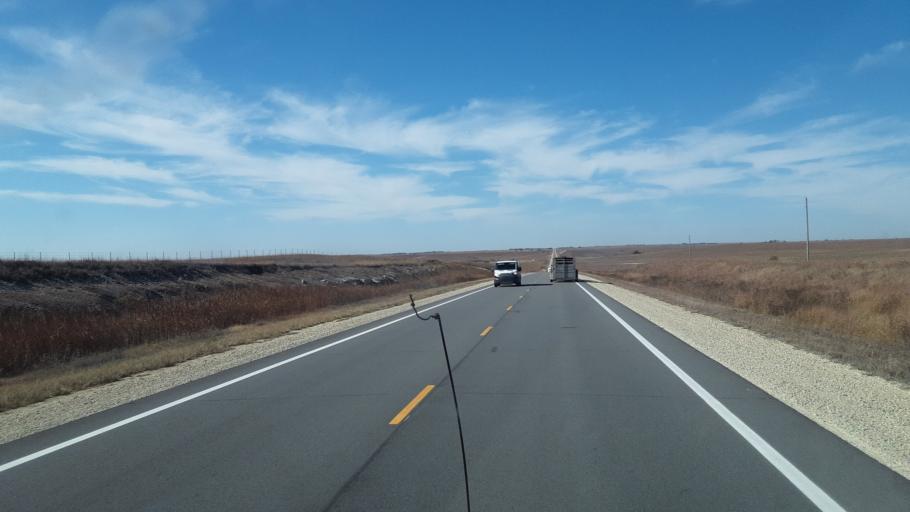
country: US
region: Kansas
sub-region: Chase County
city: Cottonwood Falls
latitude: 38.3627
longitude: -96.7398
